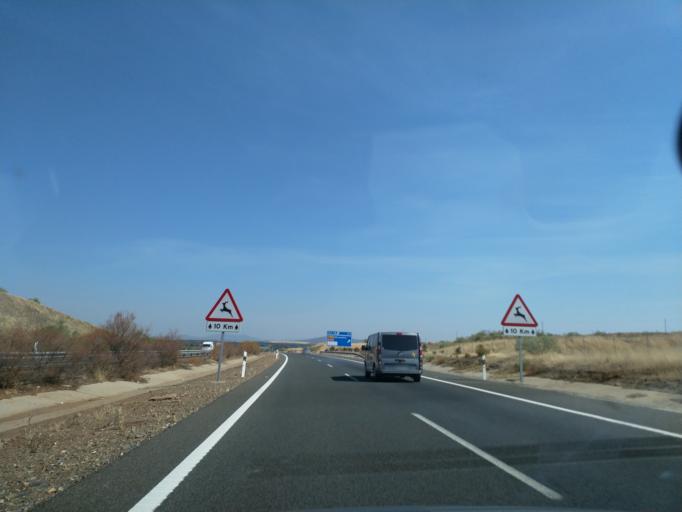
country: ES
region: Extremadura
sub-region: Provincia de Badajoz
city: Merida
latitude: 38.9673
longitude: -6.3374
